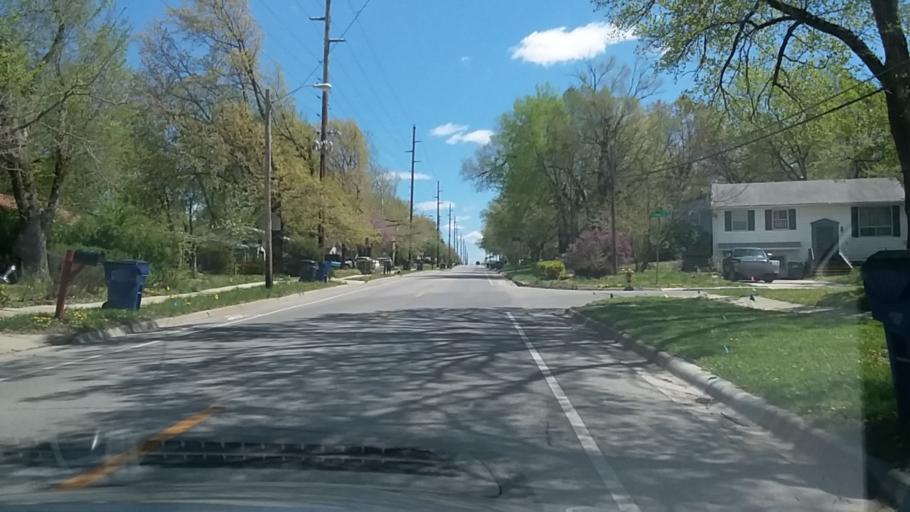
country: US
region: Kansas
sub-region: Douglas County
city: Lawrence
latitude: 38.9500
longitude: -95.2181
